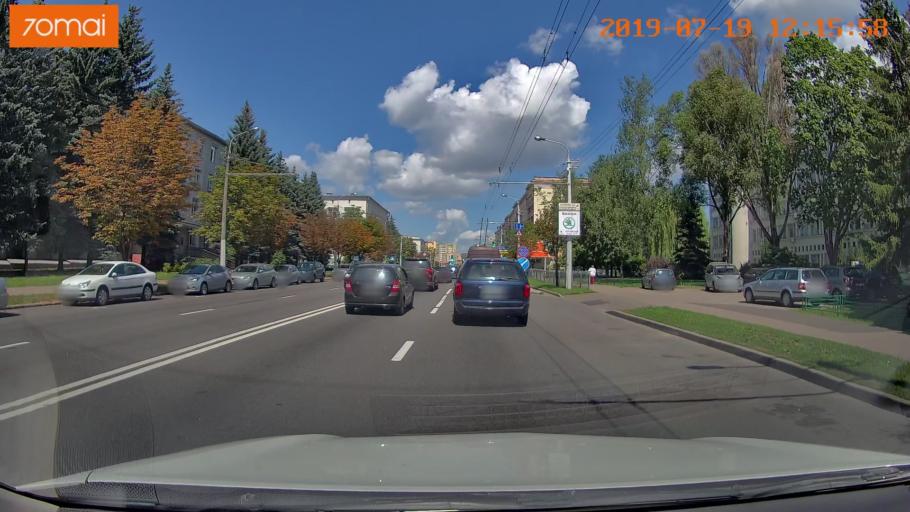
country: BY
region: Minsk
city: Minsk
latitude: 53.9197
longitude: 27.6029
